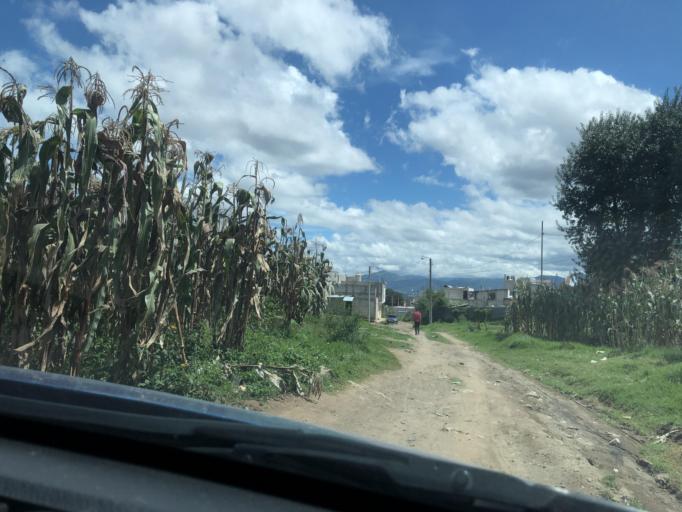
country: GT
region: Quetzaltenango
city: Quetzaltenango
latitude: 14.8385
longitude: -91.5456
